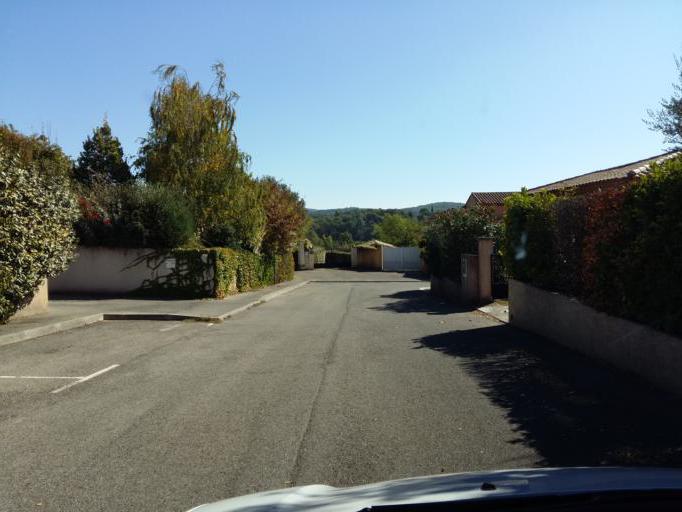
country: FR
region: Provence-Alpes-Cote d'Azur
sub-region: Departement du Vaucluse
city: Pertuis
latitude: 43.7215
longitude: 5.5396
